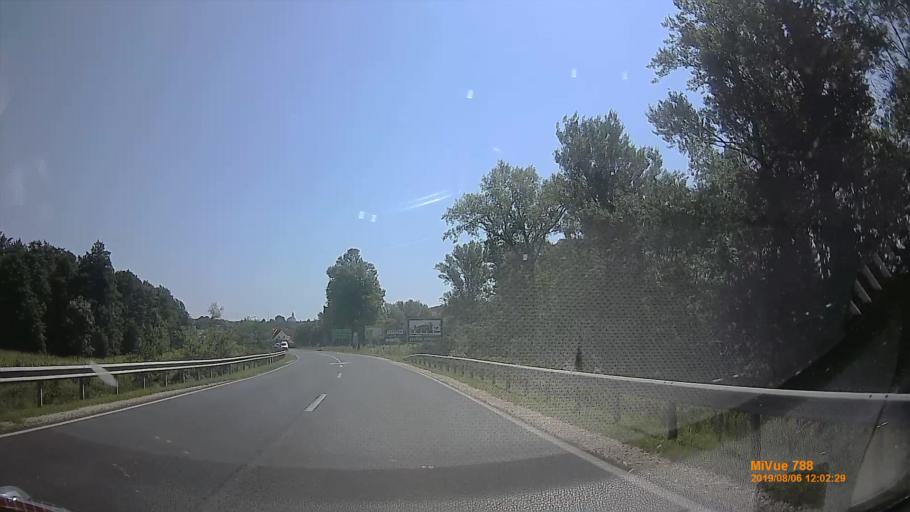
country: HU
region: Vas
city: Vasvar
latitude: 47.0558
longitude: 16.7854
